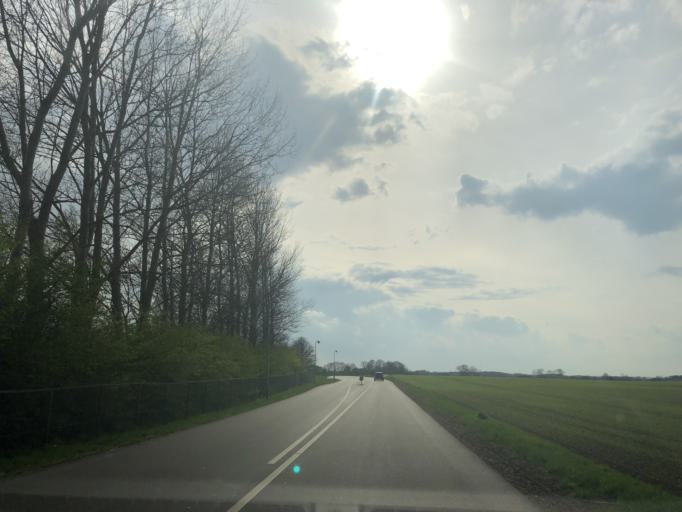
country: DK
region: Zealand
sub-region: Roskilde Kommune
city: Gundsomagle
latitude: 55.7072
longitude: 12.1567
